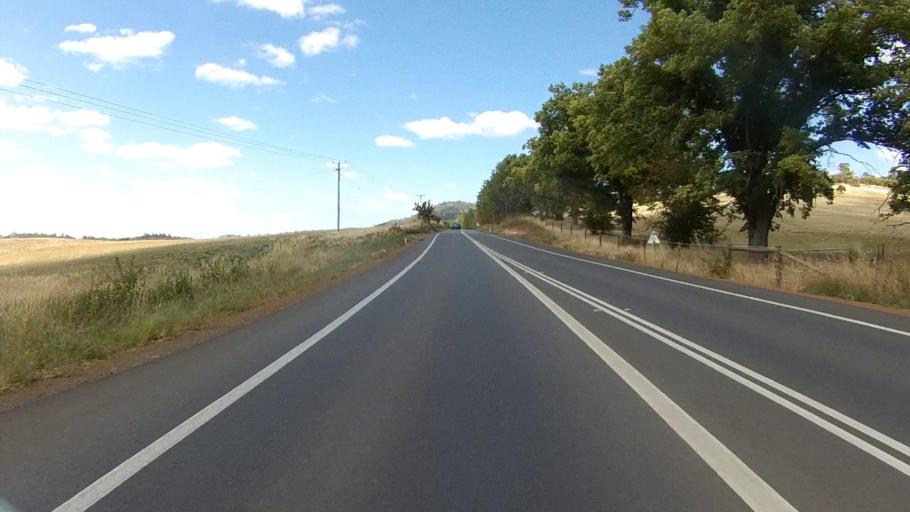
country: AU
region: Tasmania
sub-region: Clarence
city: Cambridge
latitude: -42.8042
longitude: 147.4230
